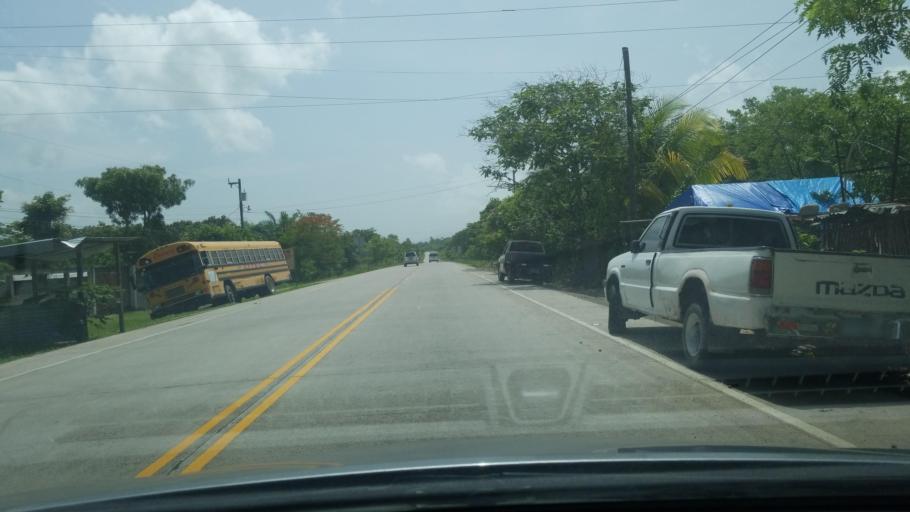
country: HN
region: Copan
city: Florida
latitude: 15.0462
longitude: -88.8081
